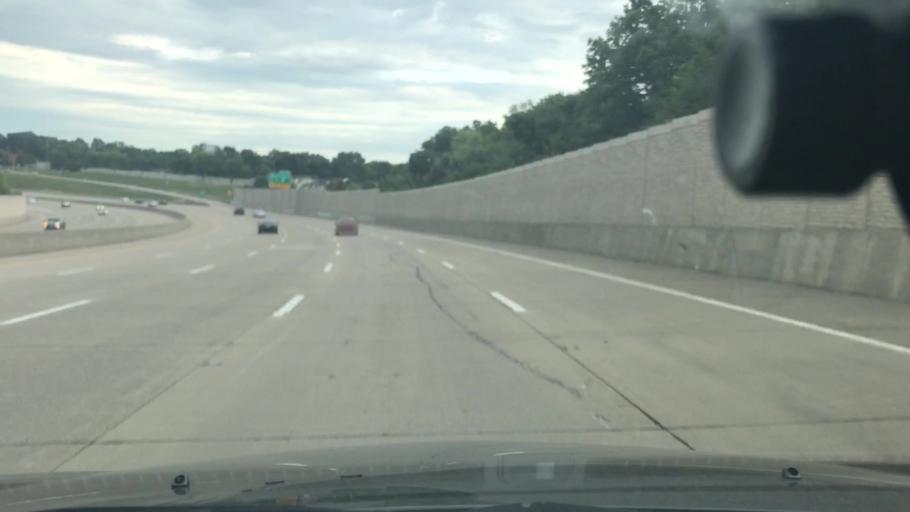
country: US
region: Missouri
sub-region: Saint Louis County
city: Maryland Heights
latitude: 38.6981
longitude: -90.4706
